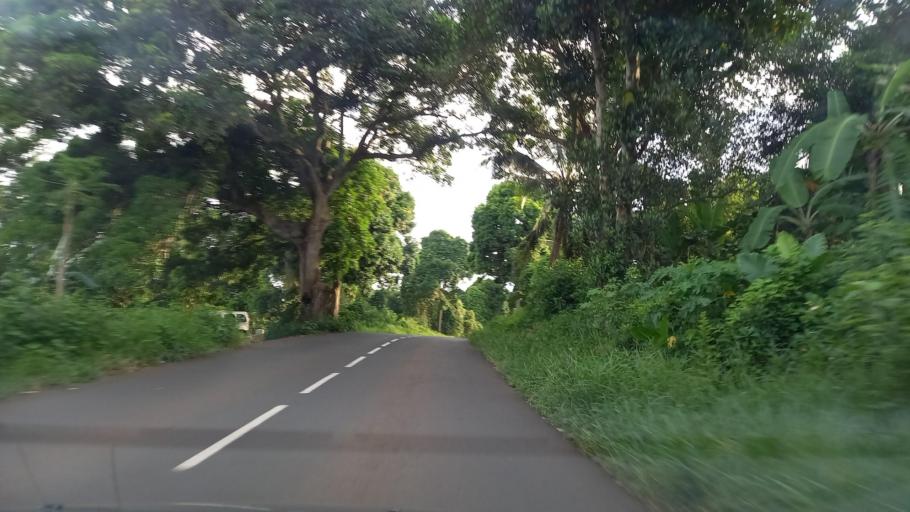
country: YT
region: M'Tsangamouji
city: M'Tsangamouji
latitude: -12.7441
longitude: 45.1152
